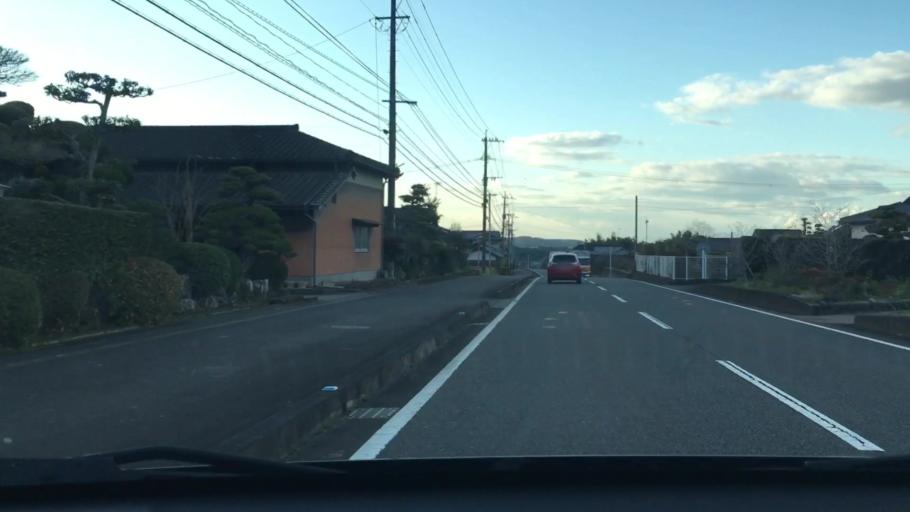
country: JP
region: Oita
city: Bungo-Takada-shi
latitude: 33.5026
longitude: 131.3705
